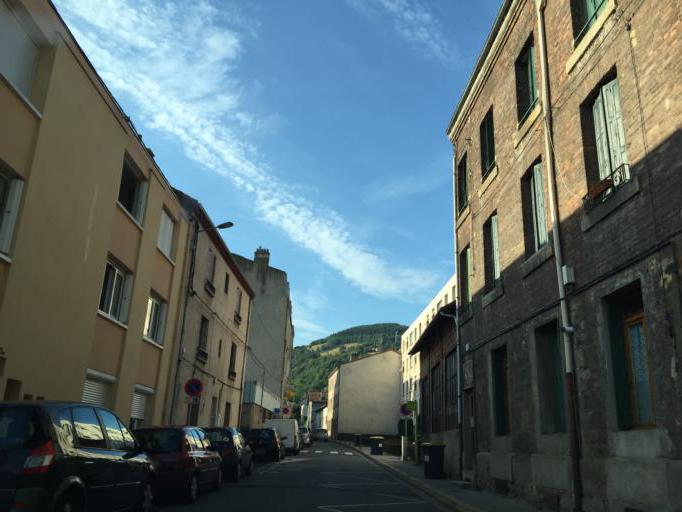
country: FR
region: Rhone-Alpes
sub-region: Departement de la Loire
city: Saint-Jean-Bonnefonds
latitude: 45.4304
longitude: 4.4334
